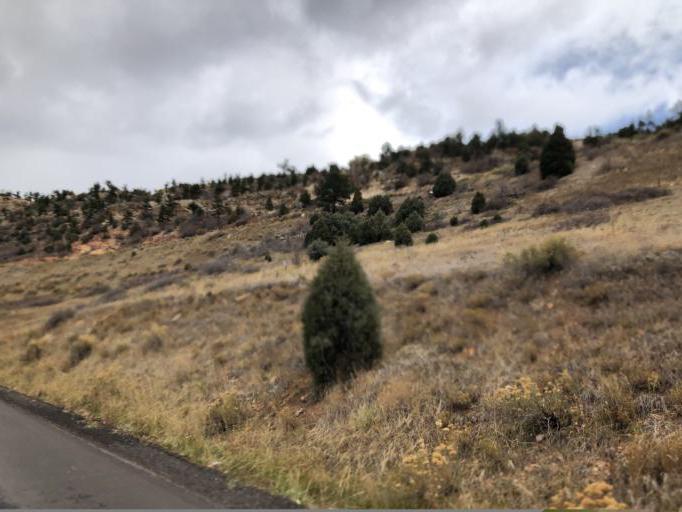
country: US
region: Colorado
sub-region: Jefferson County
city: West Pleasant View
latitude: 39.6760
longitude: -105.1944
